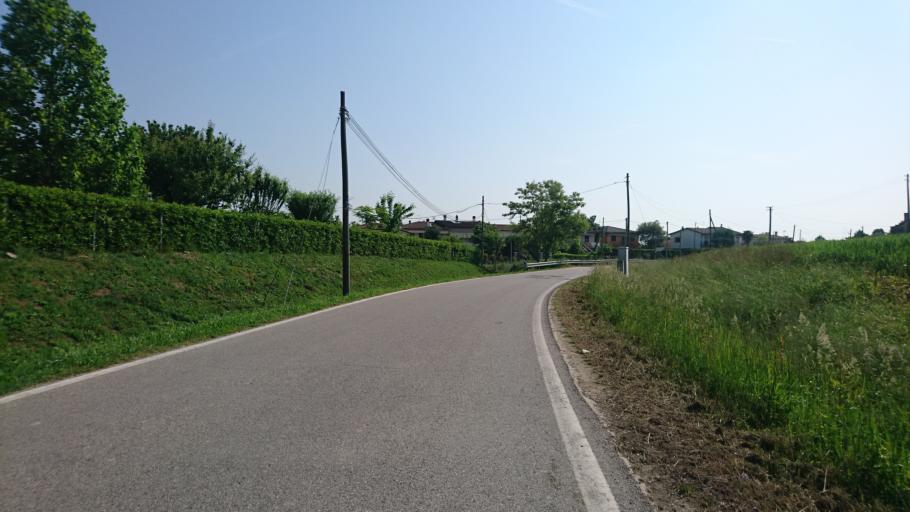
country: IT
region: Veneto
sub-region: Provincia di Venezia
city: Vigonovo
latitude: 45.3701
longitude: 12.0151
